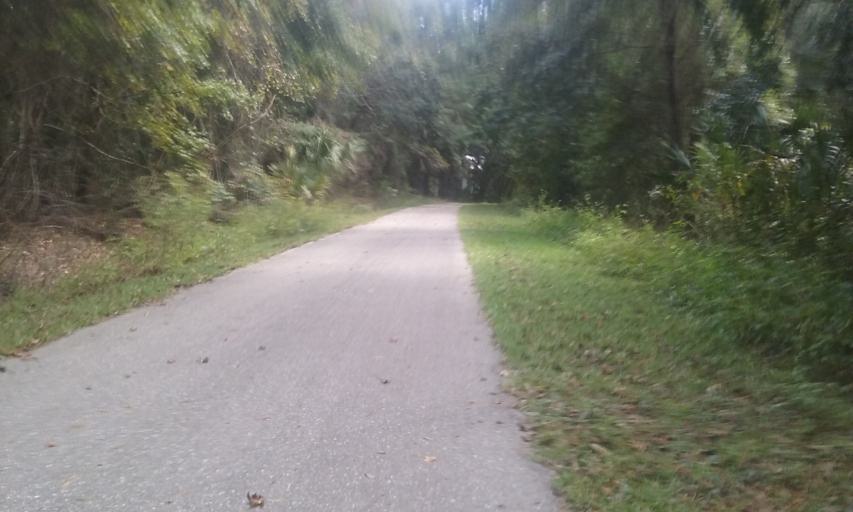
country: US
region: Florida
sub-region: Alachua County
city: Hawthorne
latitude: 29.5935
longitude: -82.1326
